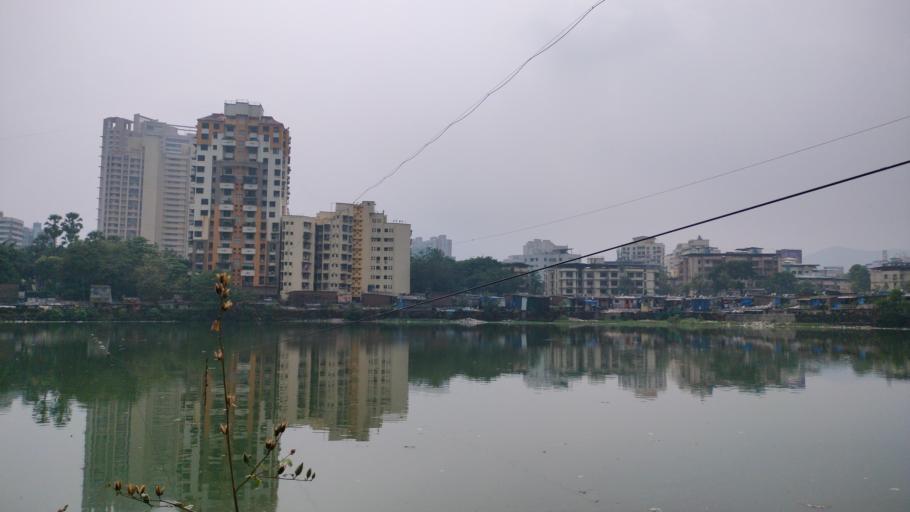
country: IN
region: Maharashtra
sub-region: Thane
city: Thane
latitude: 19.2021
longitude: 72.9691
